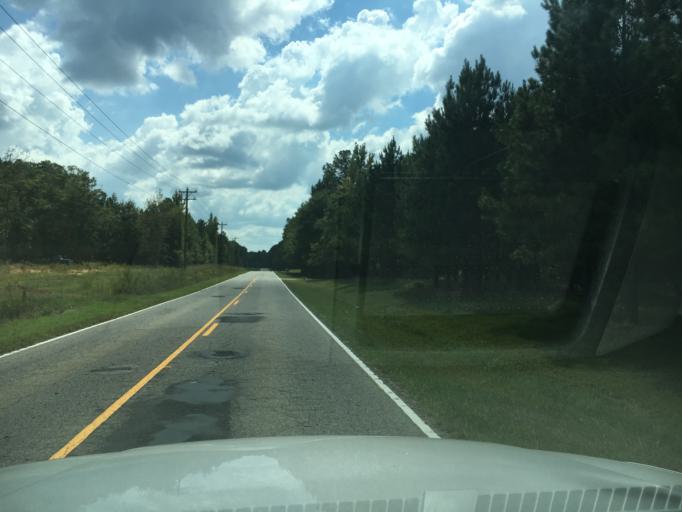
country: US
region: South Carolina
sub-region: Greenwood County
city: Greenwood
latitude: 34.1241
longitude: -82.1266
